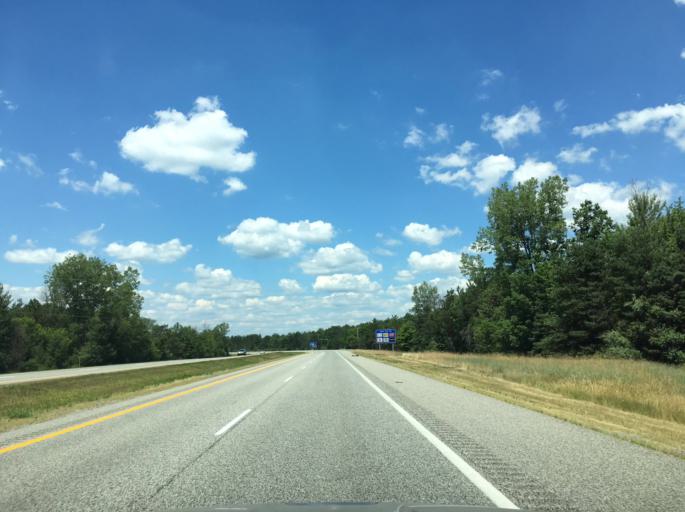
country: US
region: Michigan
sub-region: Midland County
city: Midland
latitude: 43.6534
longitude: -84.2053
